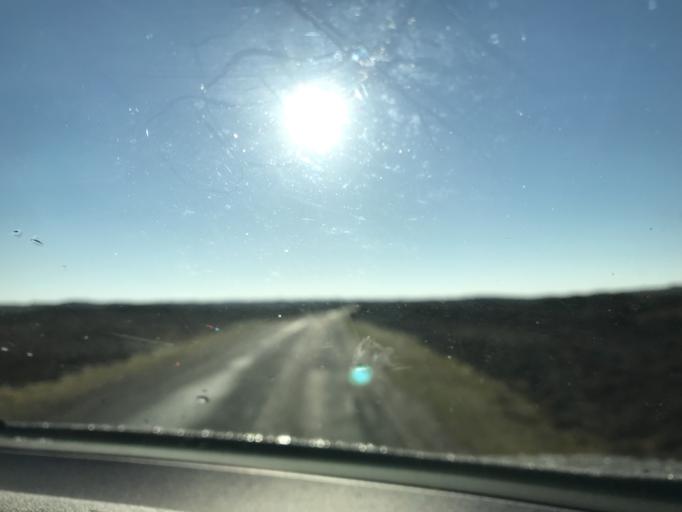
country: DK
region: Central Jutland
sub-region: Ringkobing-Skjern Kommune
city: Hvide Sande
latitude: 55.8116
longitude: 8.1775
